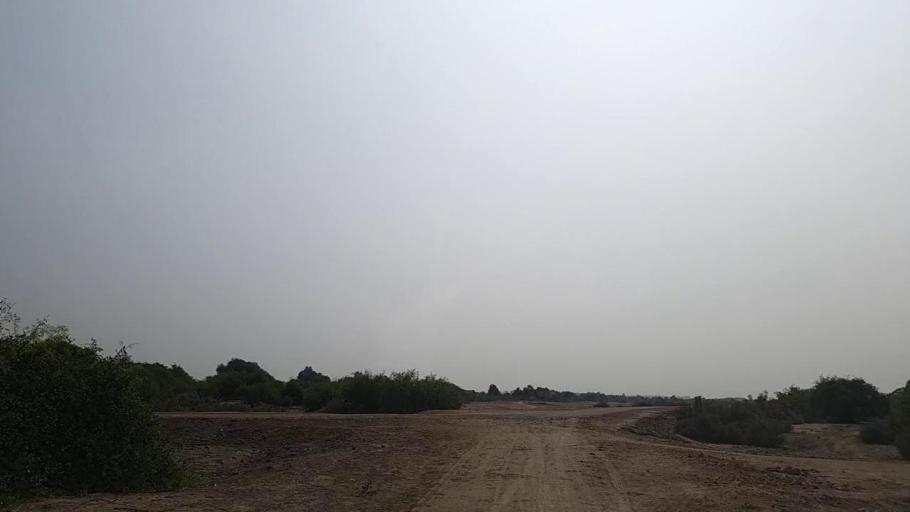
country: PK
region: Sindh
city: Mirpur Sakro
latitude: 24.6475
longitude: 67.7673
